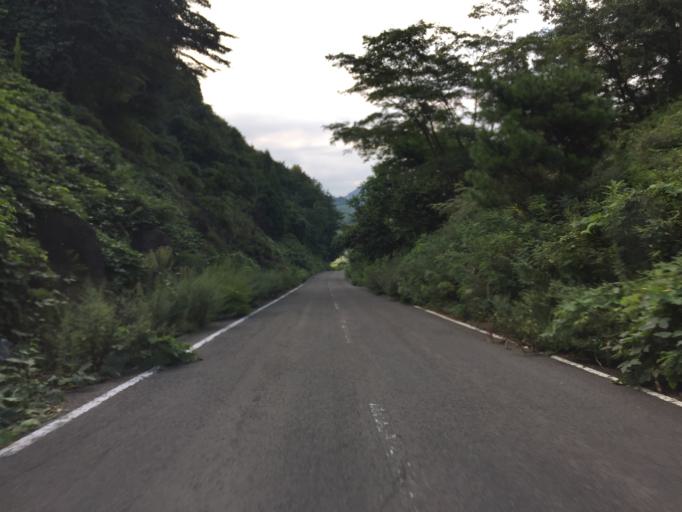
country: JP
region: Fukushima
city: Fukushima-shi
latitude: 37.6586
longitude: 140.5521
